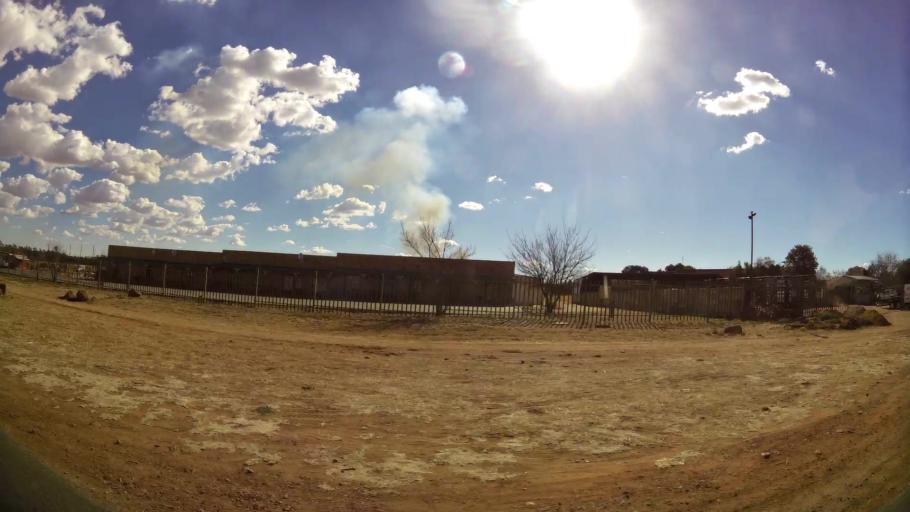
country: ZA
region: North-West
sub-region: Dr Kenneth Kaunda District Municipality
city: Klerksdorp
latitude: -26.8472
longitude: 26.6527
